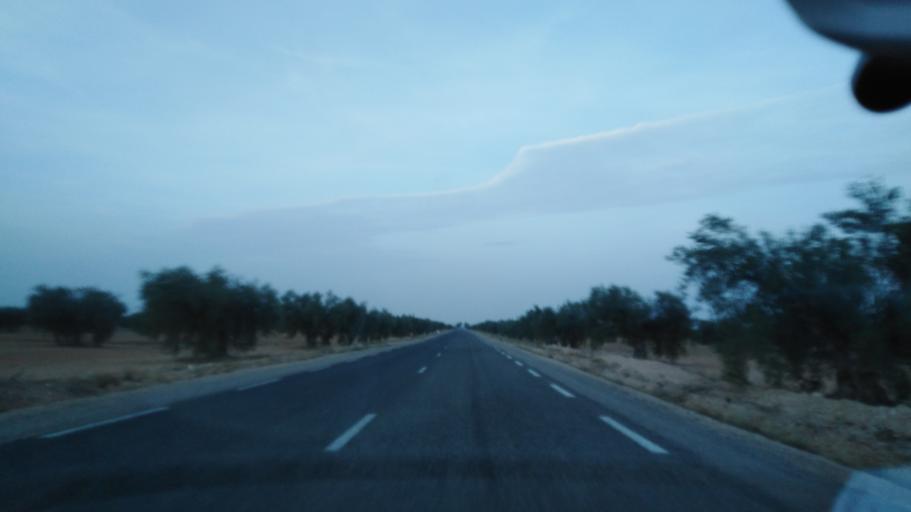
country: TN
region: Al Mahdiyah
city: Shurban
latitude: 34.9362
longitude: 10.3928
